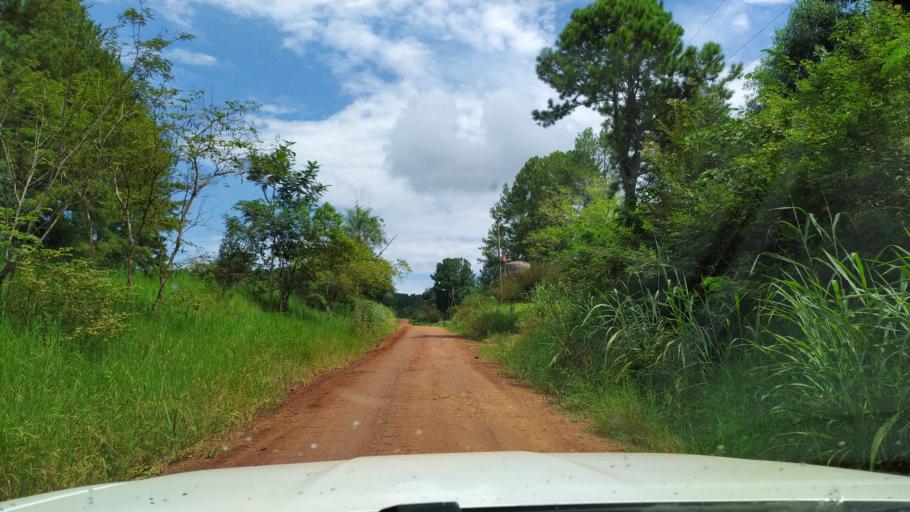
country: AR
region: Misiones
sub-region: Departamento de Eldorado
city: Eldorado
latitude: -26.4957
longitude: -54.5872
